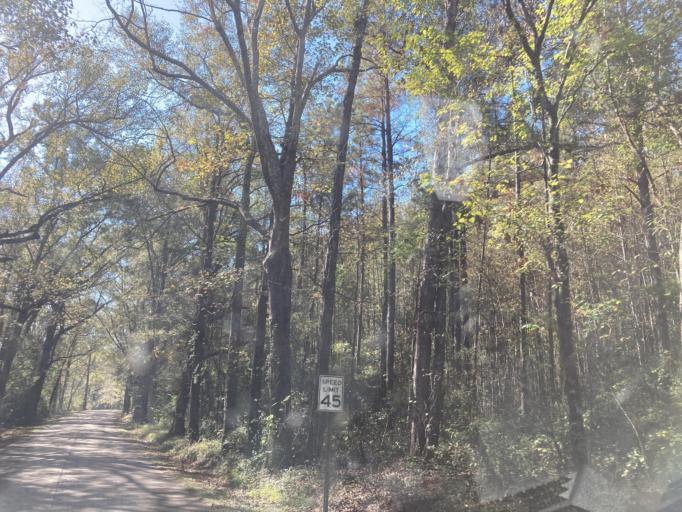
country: US
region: Mississippi
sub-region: Lamar County
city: Sumrall
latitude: 31.3314
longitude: -89.5134
